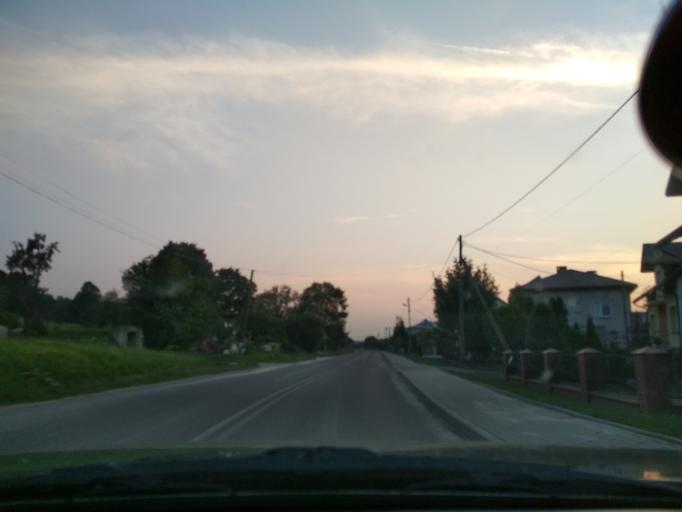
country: PL
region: Silesian Voivodeship
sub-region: Powiat zawiercianski
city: Pilica
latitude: 50.4712
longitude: 19.7401
